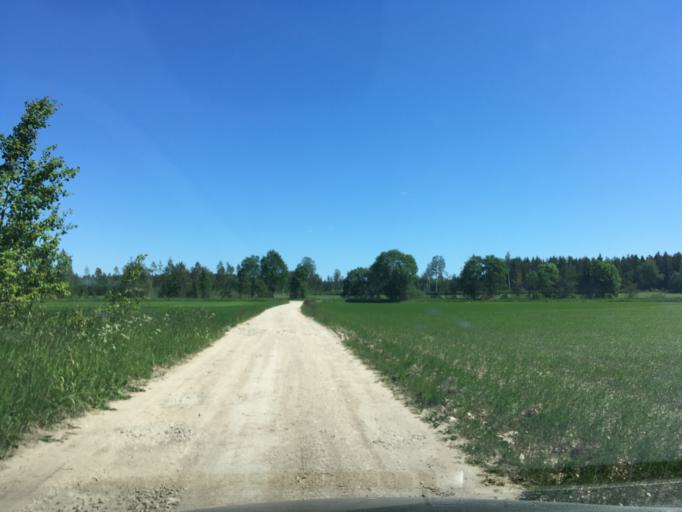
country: EE
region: Harju
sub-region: Raasiku vald
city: Raasiku
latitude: 59.1561
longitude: 25.1580
